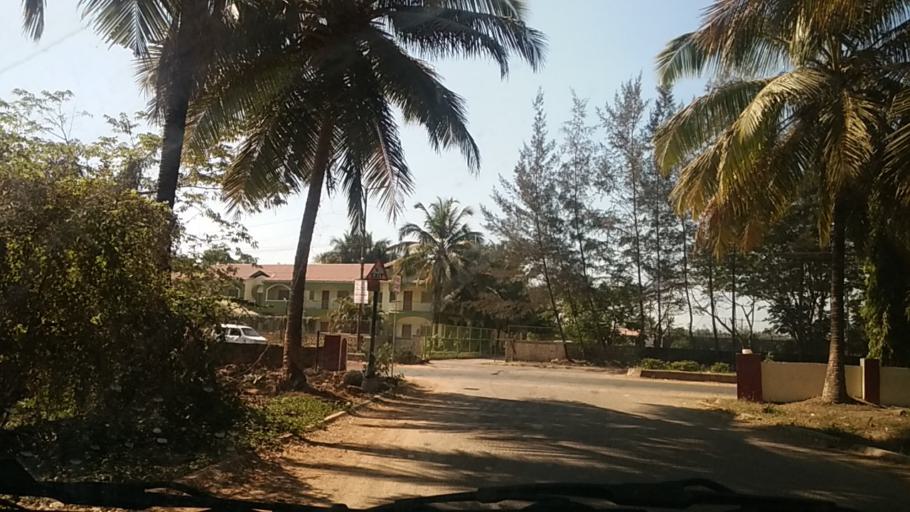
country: IN
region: Goa
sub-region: South Goa
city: Madgaon
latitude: 15.2659
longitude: 73.9717
